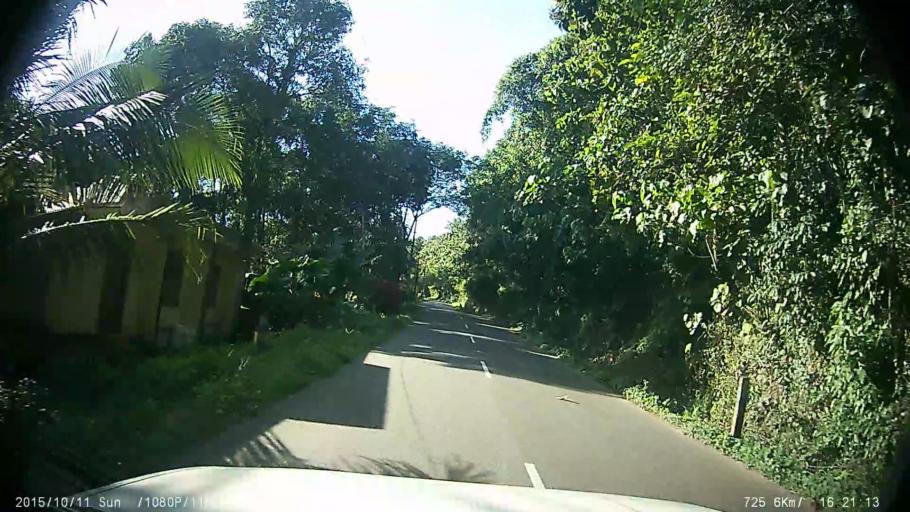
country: IN
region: Kerala
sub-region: Kottayam
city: Palackattumala
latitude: 9.7515
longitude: 76.6016
